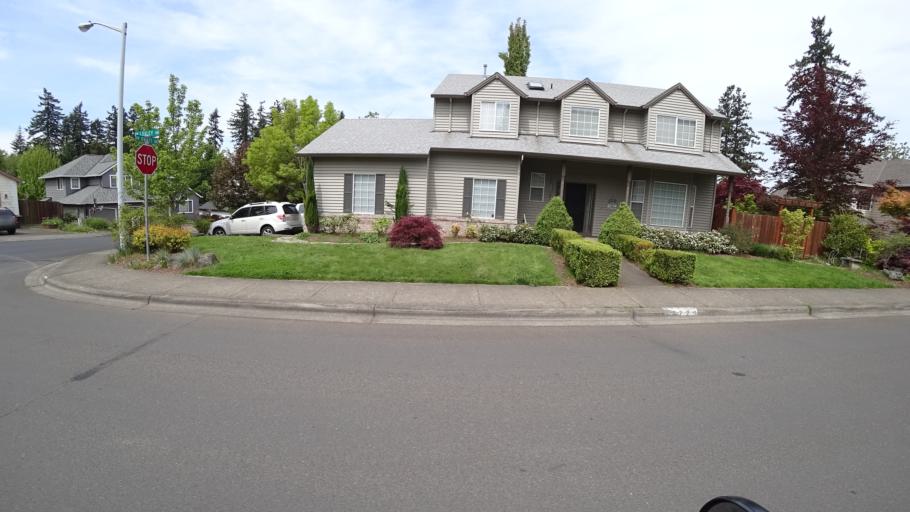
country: US
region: Oregon
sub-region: Washington County
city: Aloha
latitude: 45.4633
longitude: -122.8599
